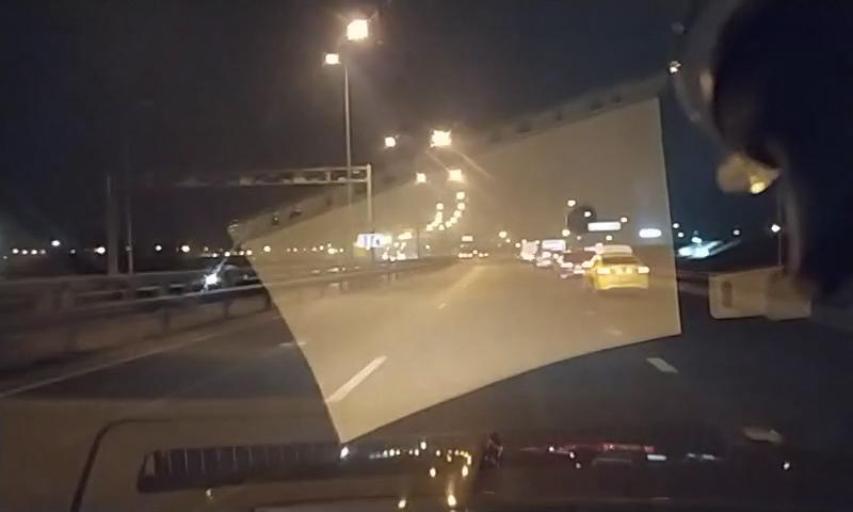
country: RU
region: Leningrad
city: Bugry
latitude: 60.0949
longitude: 30.3757
